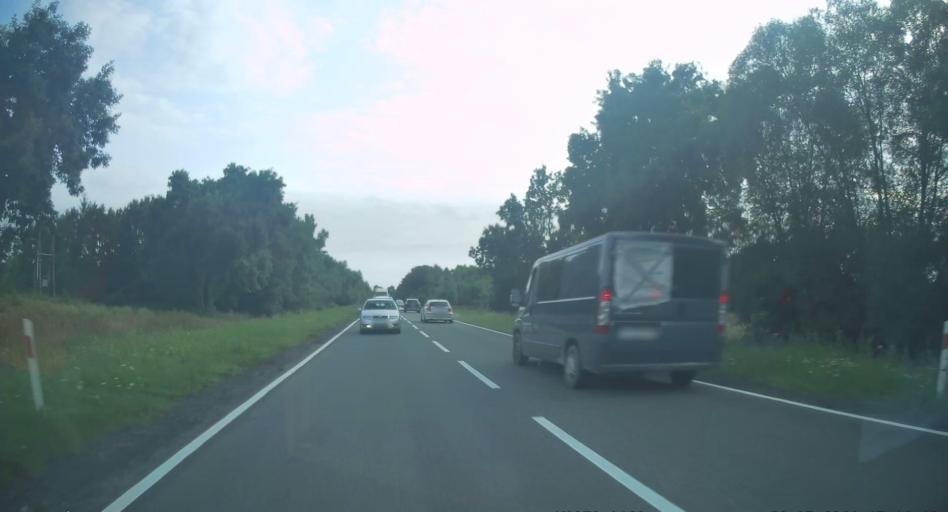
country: PL
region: Silesian Voivodeship
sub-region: Powiat czestochowski
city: Klomnice
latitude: 50.9351
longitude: 19.3841
